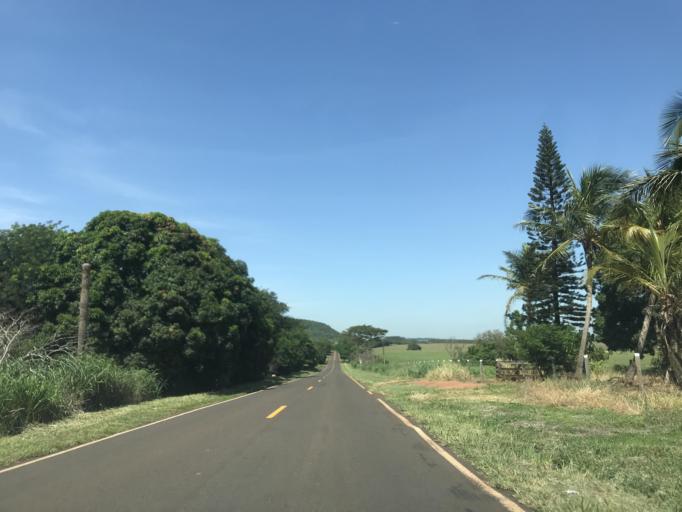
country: BR
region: Parana
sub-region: Terra Rica
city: Terra Rica
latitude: -22.7659
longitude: -52.6400
